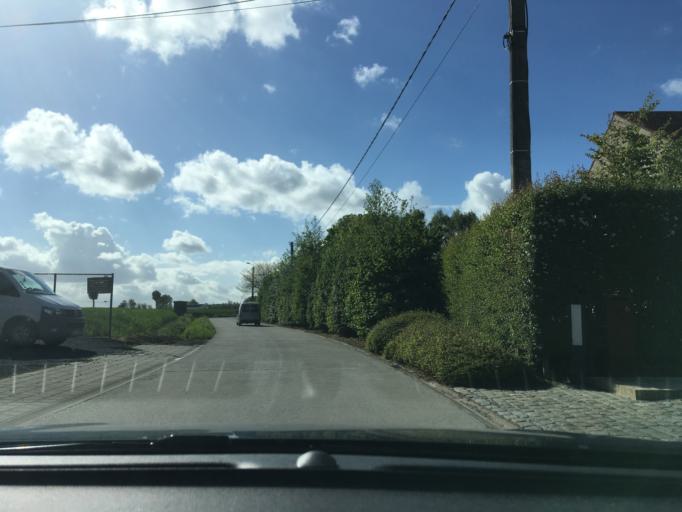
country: BE
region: Flanders
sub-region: Provincie West-Vlaanderen
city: Hooglede
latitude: 50.9993
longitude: 3.0793
